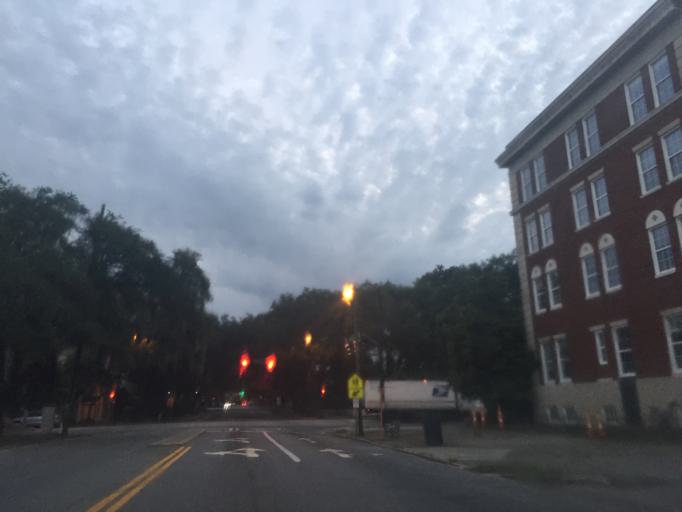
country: US
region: Georgia
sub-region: Chatham County
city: Savannah
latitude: 32.0723
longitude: -81.0865
